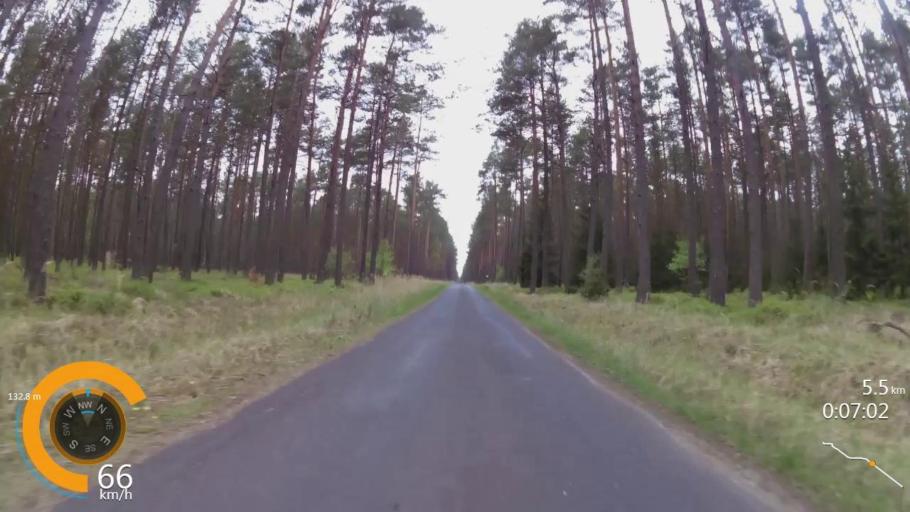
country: PL
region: West Pomeranian Voivodeship
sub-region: Powiat drawski
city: Wierzchowo
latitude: 53.4940
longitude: 16.1656
